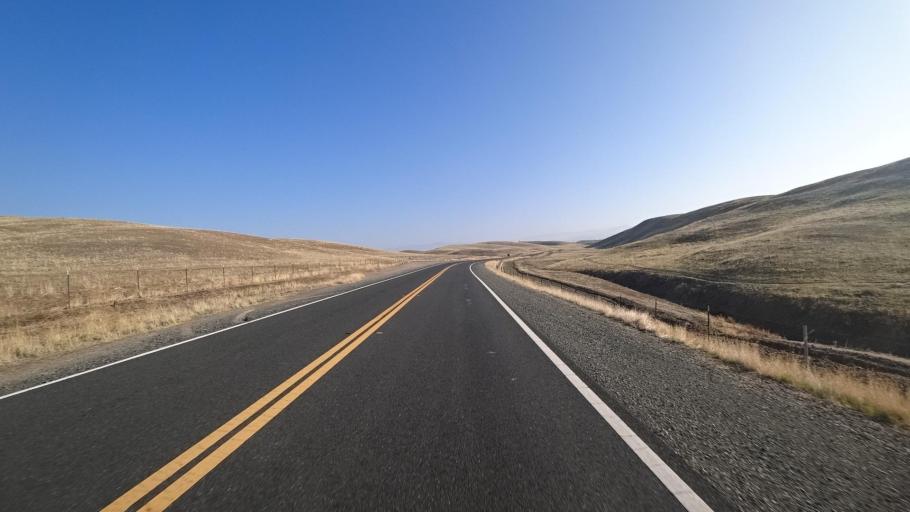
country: US
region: California
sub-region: Tulare County
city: Richgrove
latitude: 35.7417
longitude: -118.9496
